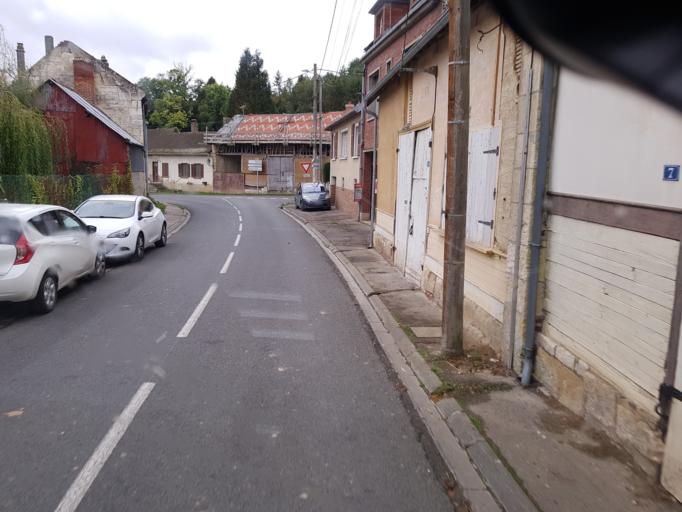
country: FR
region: Picardie
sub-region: Departement de la Somme
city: Ailly-sur-Noye
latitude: 49.7002
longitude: 2.3407
